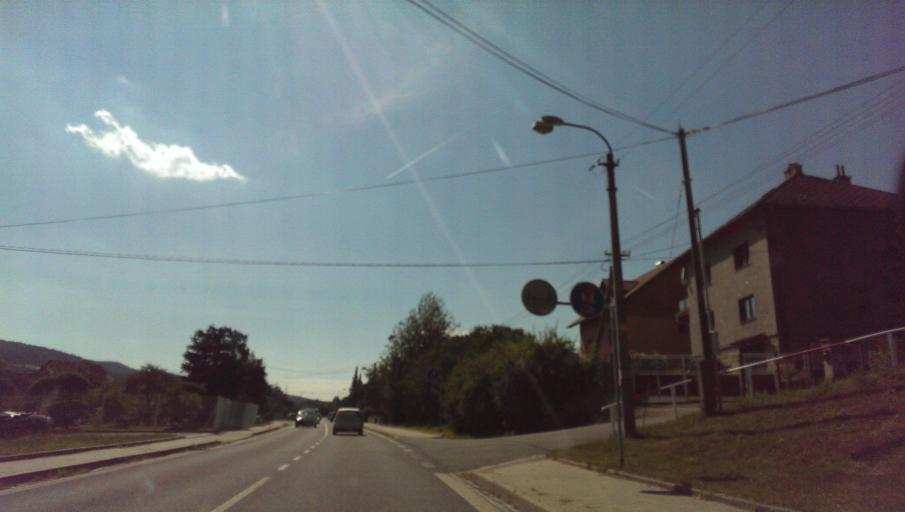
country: CZ
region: Zlin
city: Valasske Mezirici
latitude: 49.4667
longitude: 17.9413
